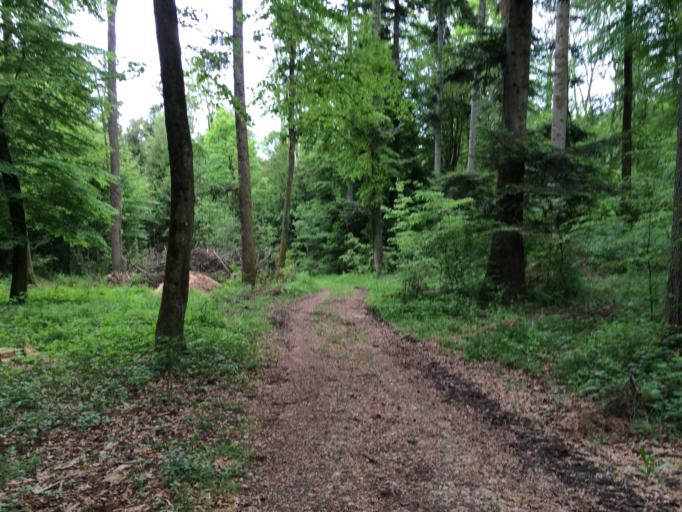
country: CH
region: Zurich
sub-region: Bezirk Uster
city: Uster / Ober-Uster
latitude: 47.3416
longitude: 8.7451
